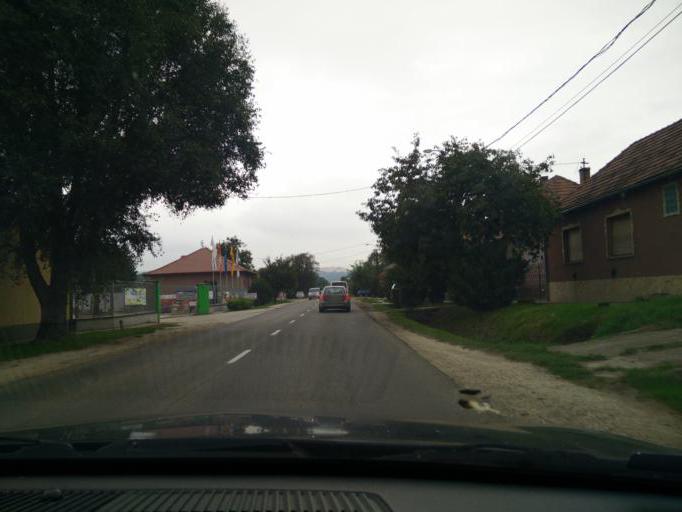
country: HU
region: Komarom-Esztergom
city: Kesztolc
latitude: 47.6860
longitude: 18.7726
